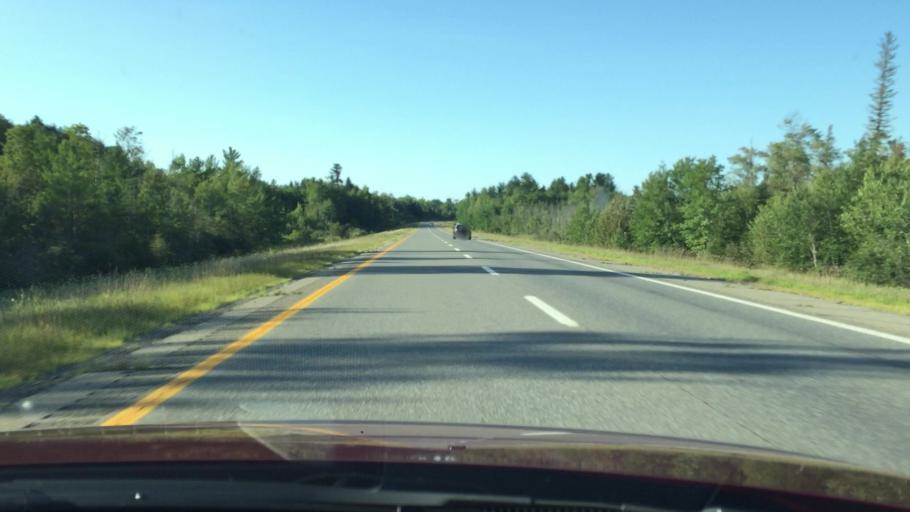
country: US
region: Maine
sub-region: Penobscot County
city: Lincoln
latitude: 45.4439
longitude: -68.5900
